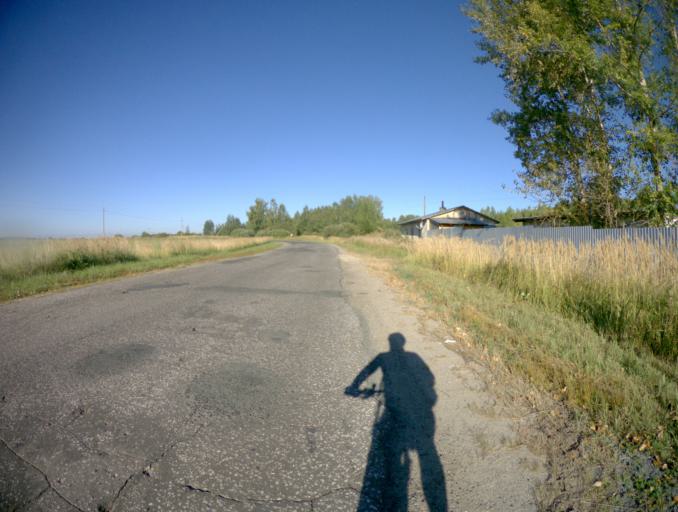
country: RU
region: Vladimir
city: Luknovo
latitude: 56.2218
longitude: 42.0231
